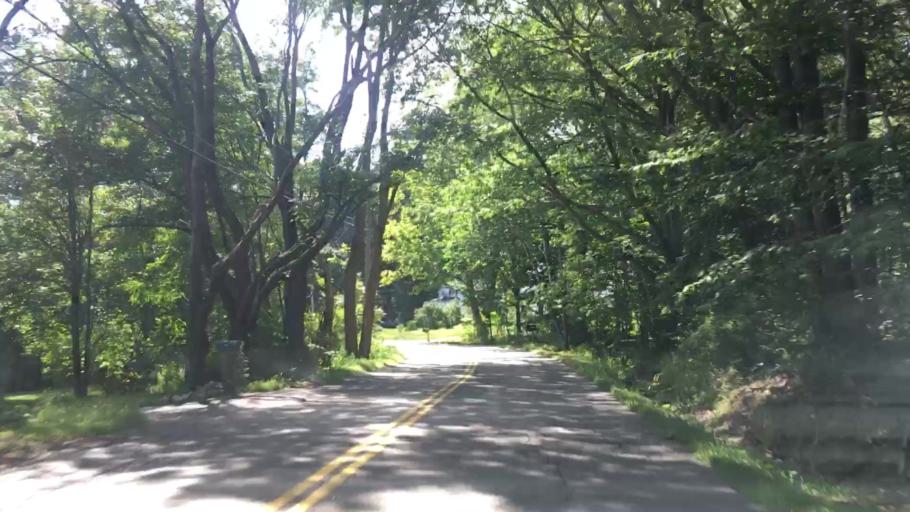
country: US
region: Maine
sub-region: Cumberland County
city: South Portland
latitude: 43.6166
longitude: -70.2589
